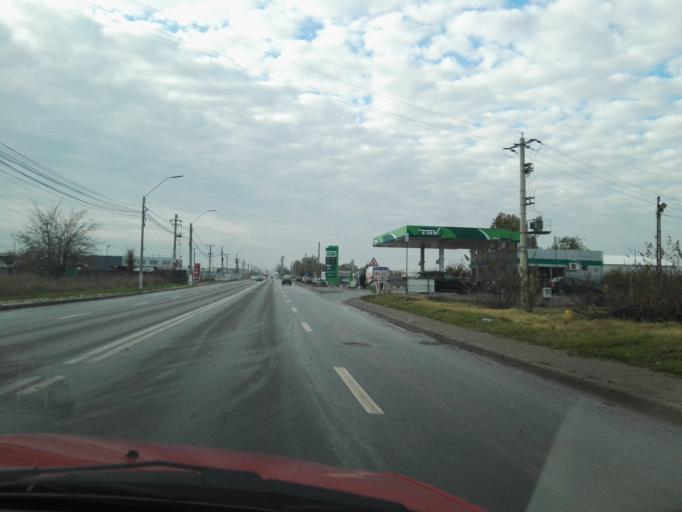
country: RO
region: Ilfov
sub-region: Comuna Magurele
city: Magurele
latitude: 44.3736
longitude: 26.0450
